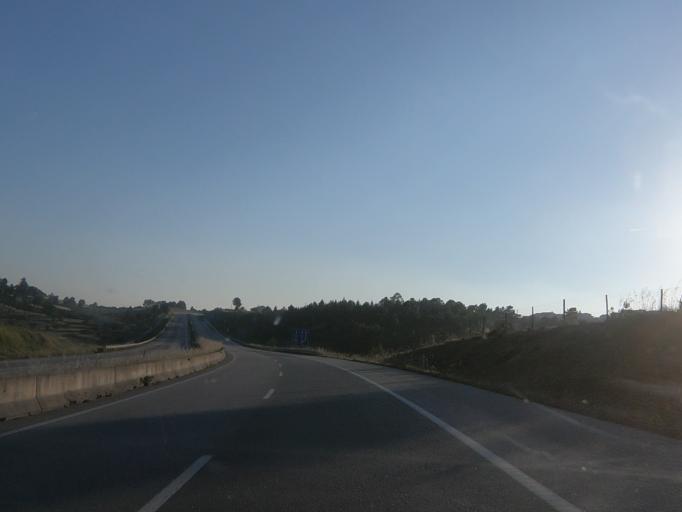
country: PT
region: Guarda
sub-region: Celorico da Beira
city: Celorico da Beira
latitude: 40.6279
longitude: -7.3867
